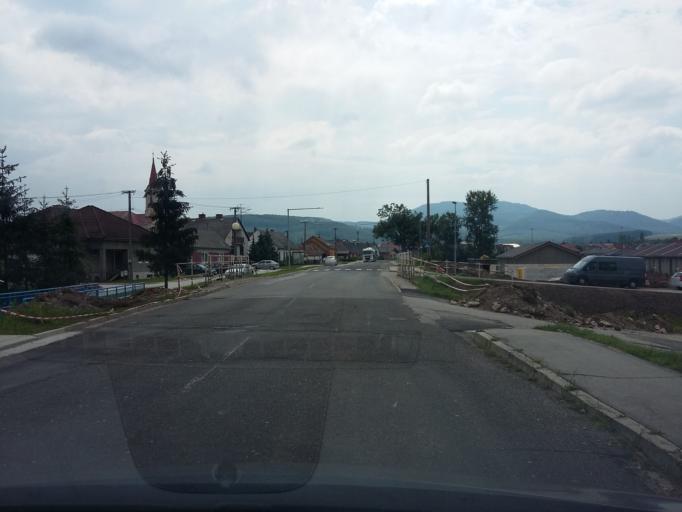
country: SK
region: Bratislavsky
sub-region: Okres Malacky
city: Malacky
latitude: 48.4624
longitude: 17.1633
